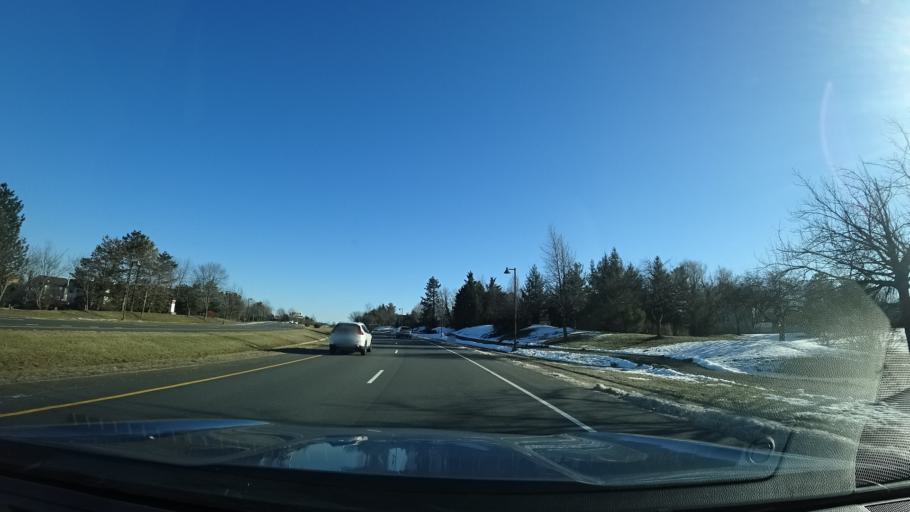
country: US
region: Virginia
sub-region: Loudoun County
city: Ashburn
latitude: 39.0459
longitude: -77.4808
